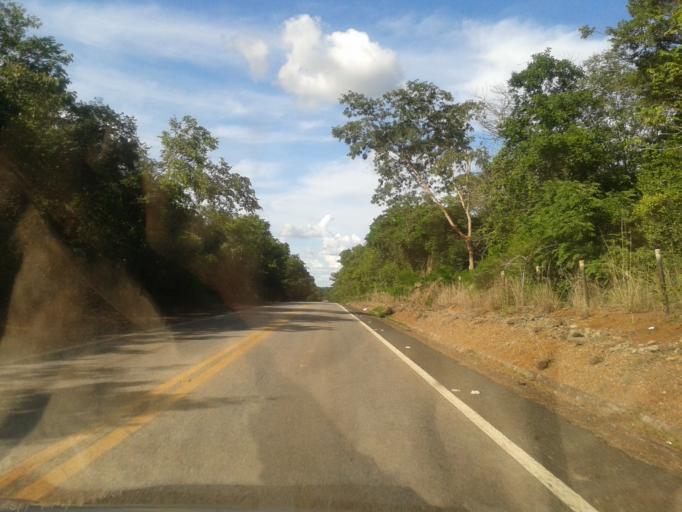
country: BR
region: Goias
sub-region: Mozarlandia
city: Mozarlandia
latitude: -14.6779
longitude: -50.5373
